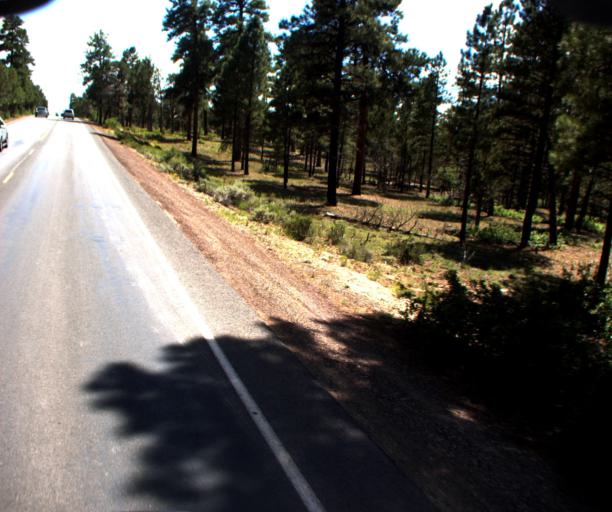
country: US
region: Arizona
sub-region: Coconino County
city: Grand Canyon
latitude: 36.0298
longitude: -112.1231
